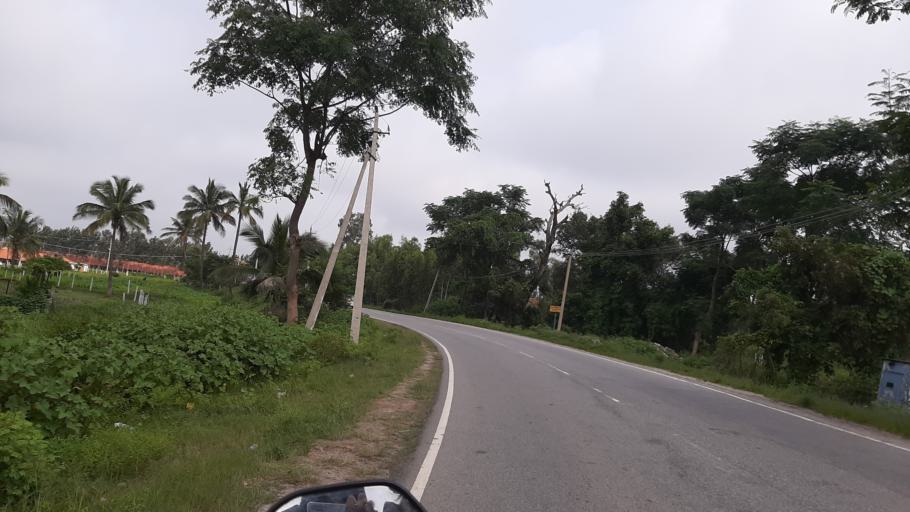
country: IN
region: Karnataka
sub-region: Bangalore Rural
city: Nelamangala
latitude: 12.9693
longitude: 77.3778
